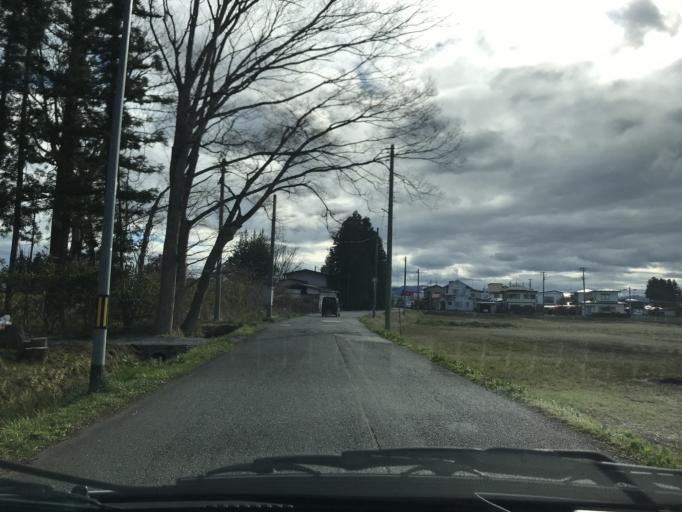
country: JP
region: Iwate
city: Mizusawa
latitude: 39.1190
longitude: 141.1322
